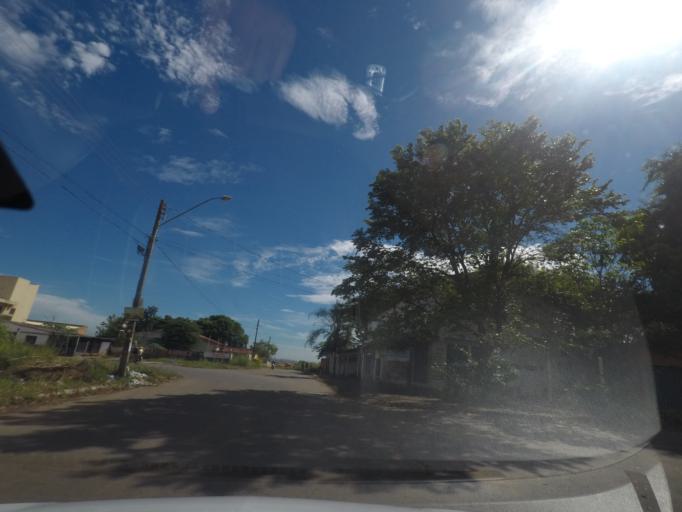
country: BR
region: Goias
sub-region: Aparecida De Goiania
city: Aparecida de Goiania
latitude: -16.8128
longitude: -49.2903
